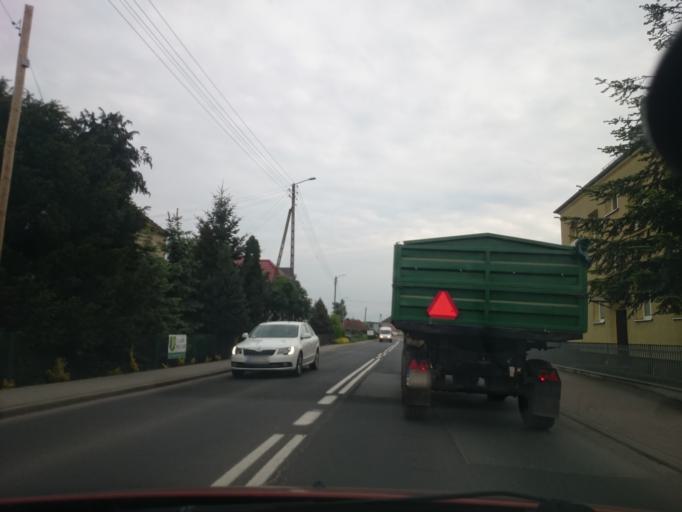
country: PL
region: Opole Voivodeship
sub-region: Powiat opolski
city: Dobrzen Wielki
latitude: 50.7634
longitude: 17.8440
